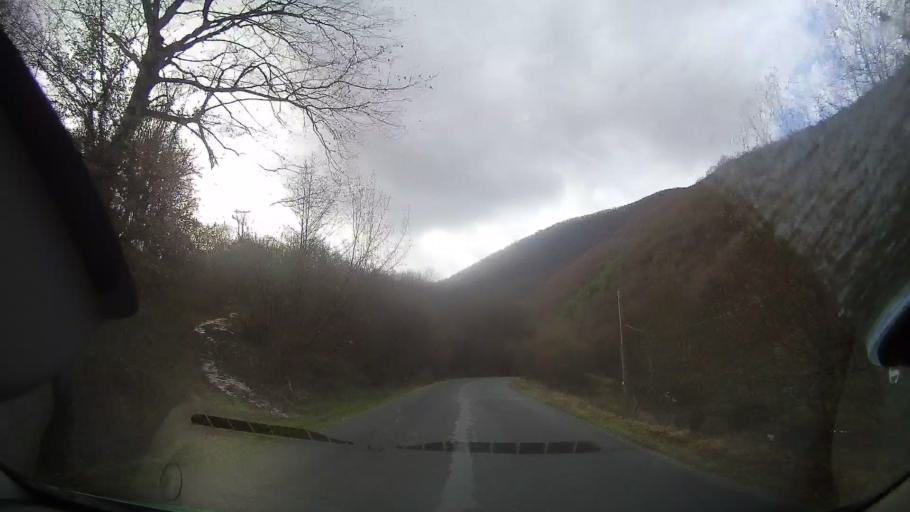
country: RO
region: Alba
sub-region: Comuna Rimetea
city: Rimetea
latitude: 46.4958
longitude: 23.5830
